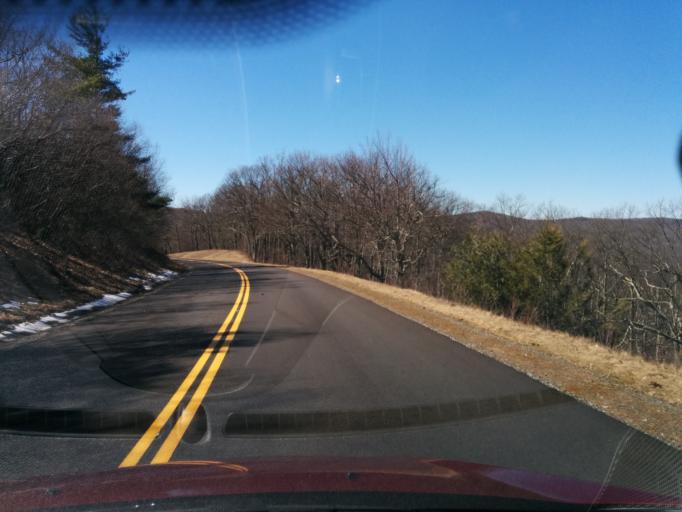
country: US
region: Virginia
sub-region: Augusta County
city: Stuarts Draft
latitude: 37.9145
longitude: -79.0746
